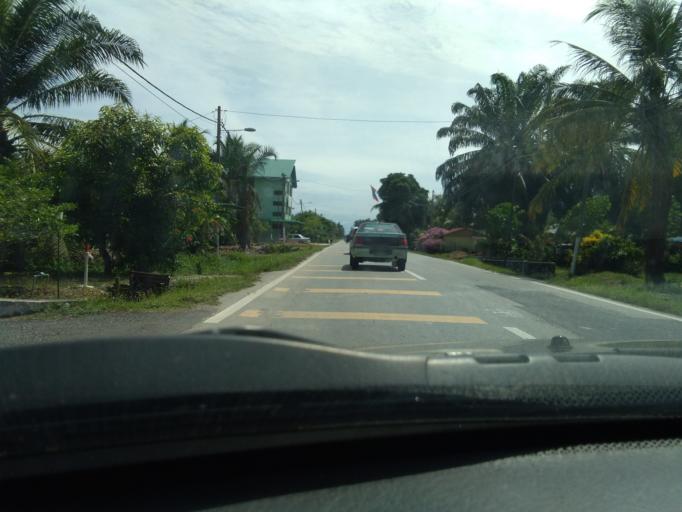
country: MY
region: Perak
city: Bagan Serai
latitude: 5.0248
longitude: 100.5529
